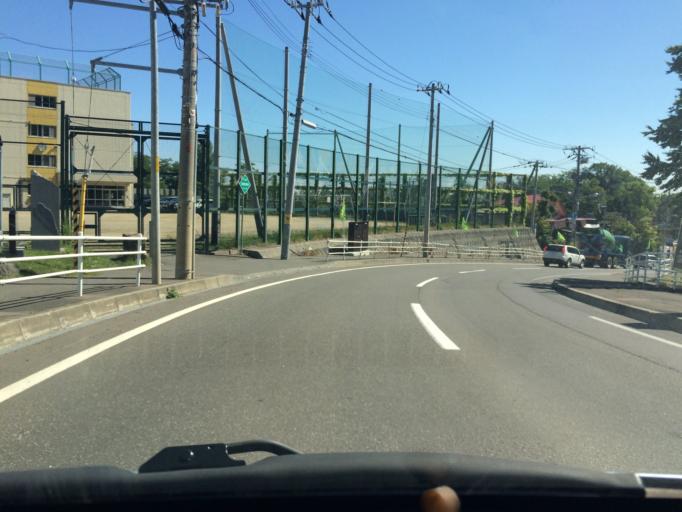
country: JP
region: Hokkaido
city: Sapporo
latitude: 43.0503
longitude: 141.2968
